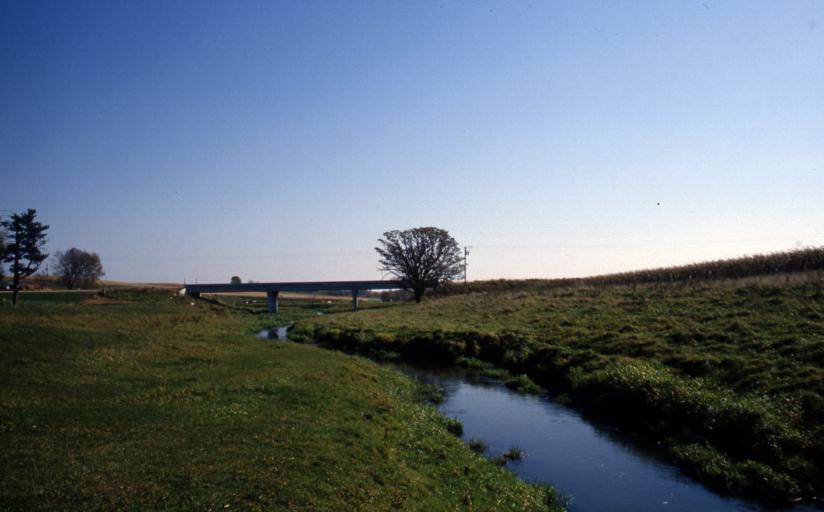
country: US
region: Minnesota
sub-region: Wabasha County
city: Elgin
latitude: 44.1214
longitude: -92.2199
